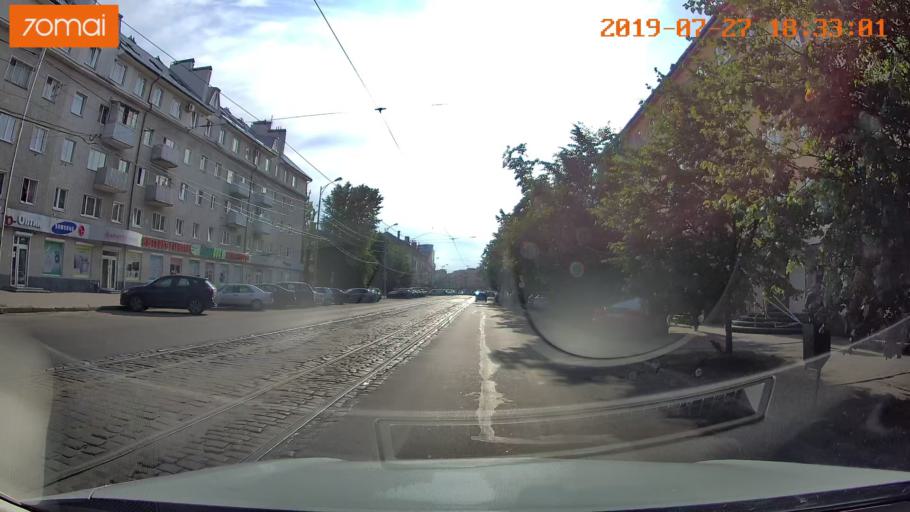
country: RU
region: Kaliningrad
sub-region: Gorod Kaliningrad
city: Kaliningrad
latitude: 54.6994
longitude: 20.5078
